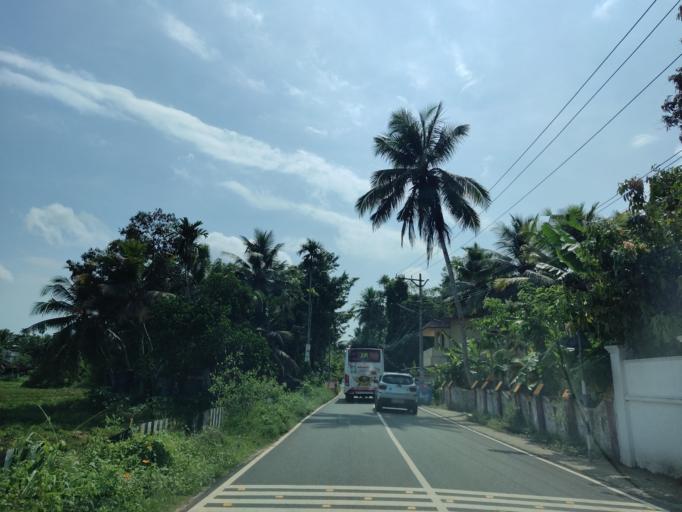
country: IN
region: Kerala
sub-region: Alappuzha
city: Mavelikara
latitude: 9.3234
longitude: 76.5214
